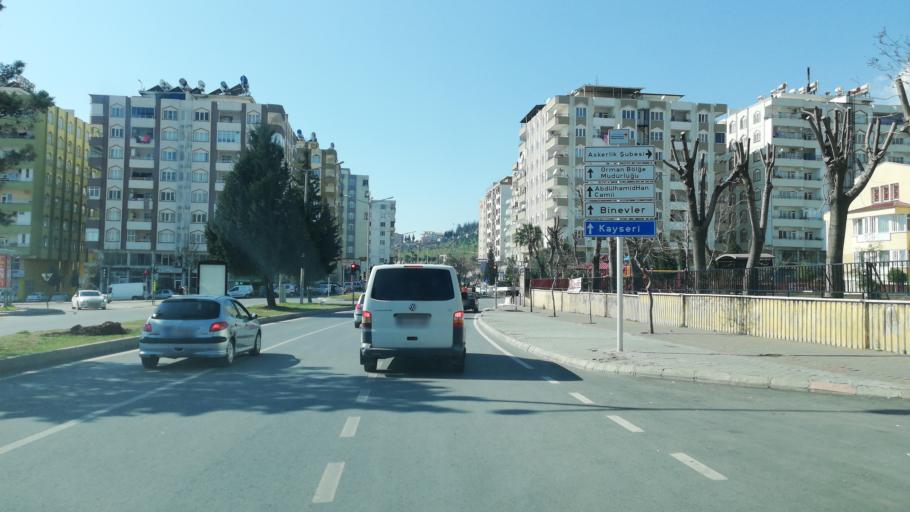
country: TR
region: Kahramanmaras
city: Kahramanmaras
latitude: 37.5714
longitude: 36.9209
